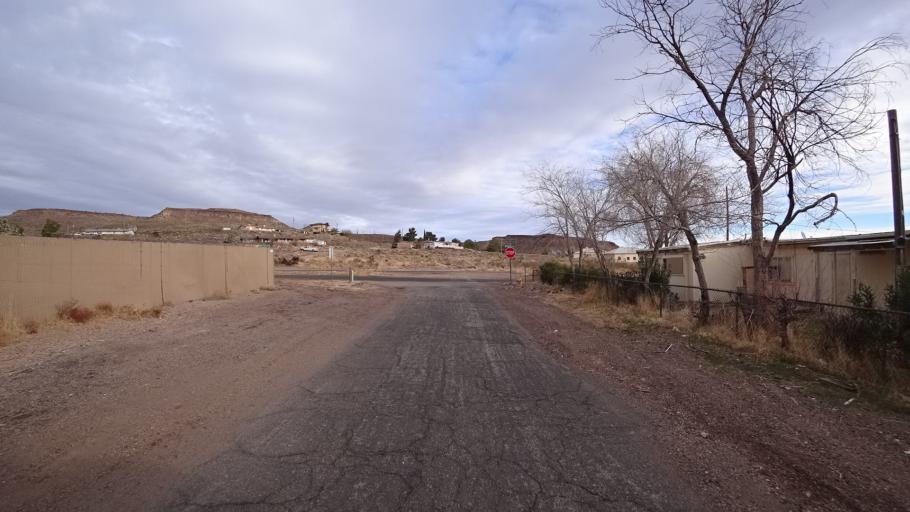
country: US
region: Arizona
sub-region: Mohave County
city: Kingman
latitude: 35.2182
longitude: -114.0533
